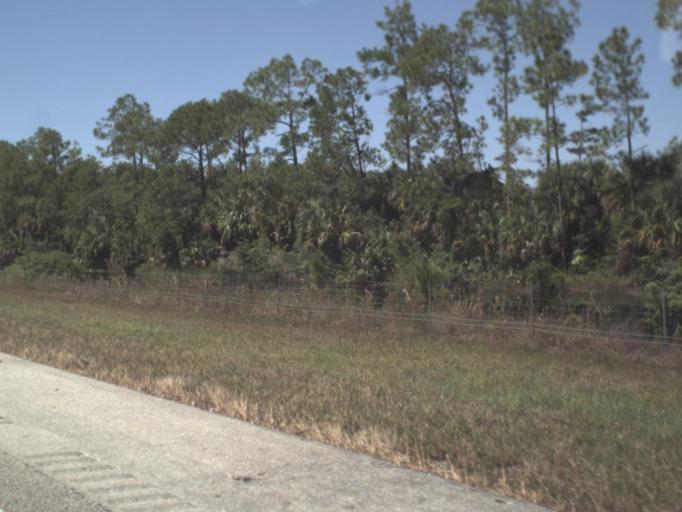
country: US
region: Florida
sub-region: Collier County
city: Golden Gate
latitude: 26.1548
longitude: -81.6352
